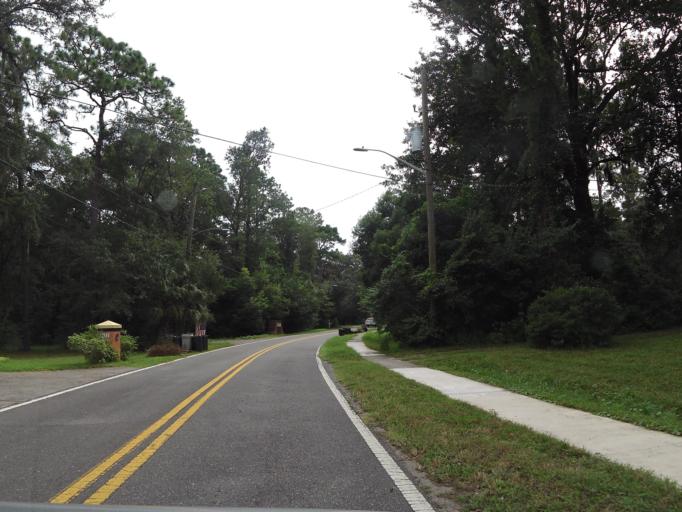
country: US
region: Florida
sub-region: Clay County
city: Bellair-Meadowbrook Terrace
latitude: 30.2600
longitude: -81.7234
